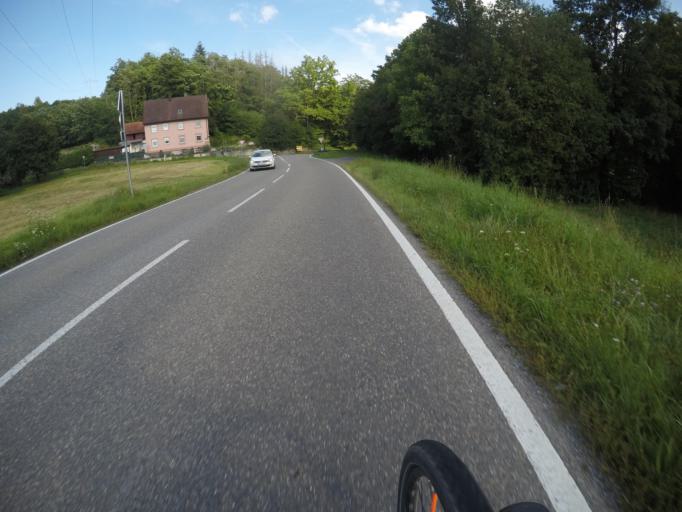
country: DE
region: Baden-Wuerttemberg
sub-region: Karlsruhe Region
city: Niefern-Oschelbronn
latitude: 48.9376
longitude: 8.7832
